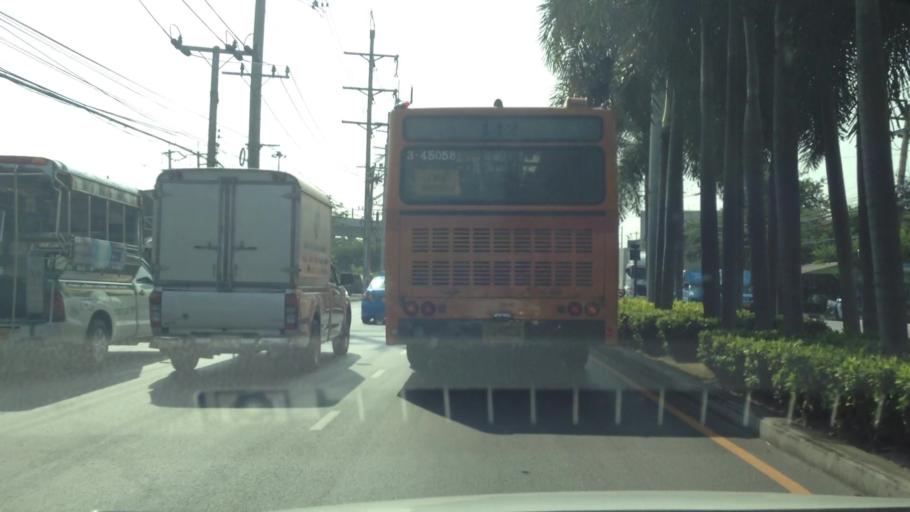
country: TH
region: Samut Prakan
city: Samut Prakan
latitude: 13.5771
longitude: 100.6037
